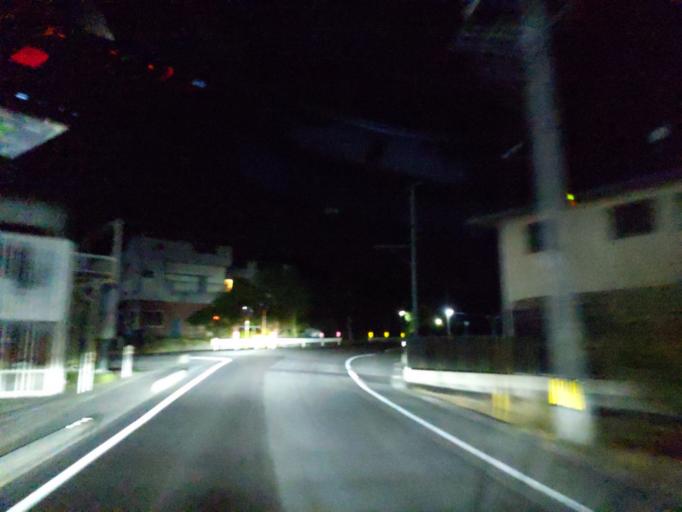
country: JP
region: Okayama
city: Okayama-shi
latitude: 34.7041
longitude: 133.9505
